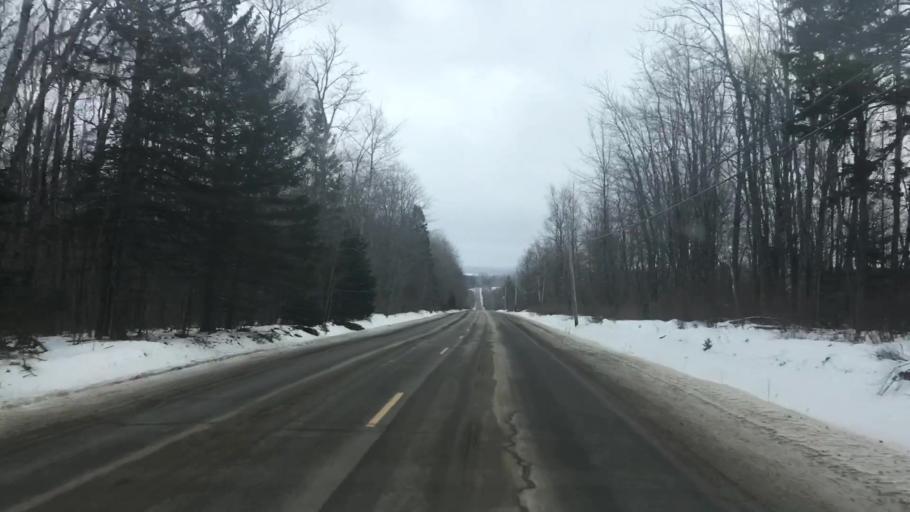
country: US
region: Maine
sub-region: Washington County
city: East Machias
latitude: 44.9753
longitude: -67.4506
